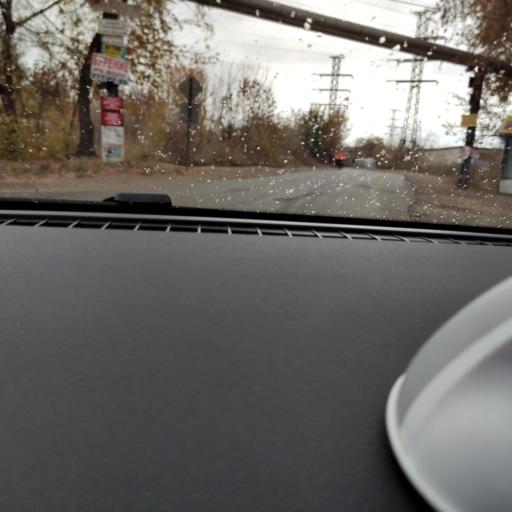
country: RU
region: Samara
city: Petra-Dubrava
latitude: 53.2956
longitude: 50.2898
